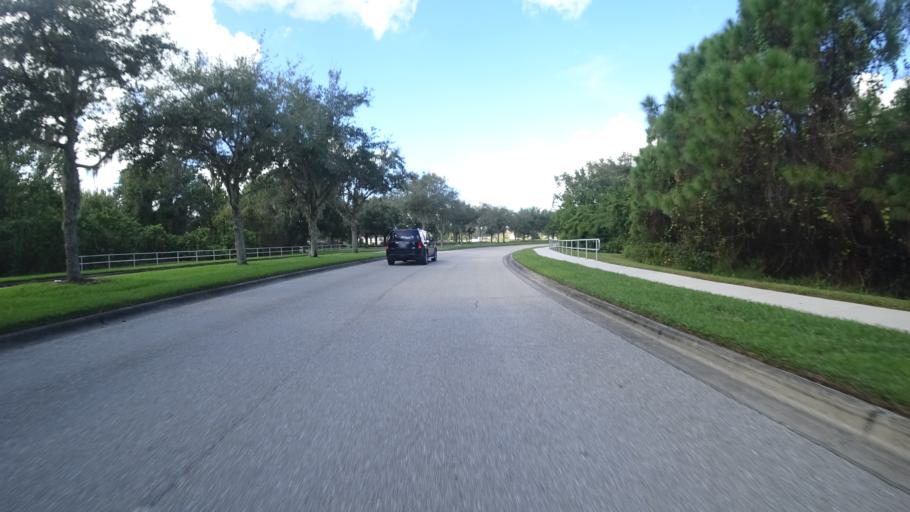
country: US
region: Florida
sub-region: Manatee County
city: Ellenton
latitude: 27.5007
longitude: -82.3705
